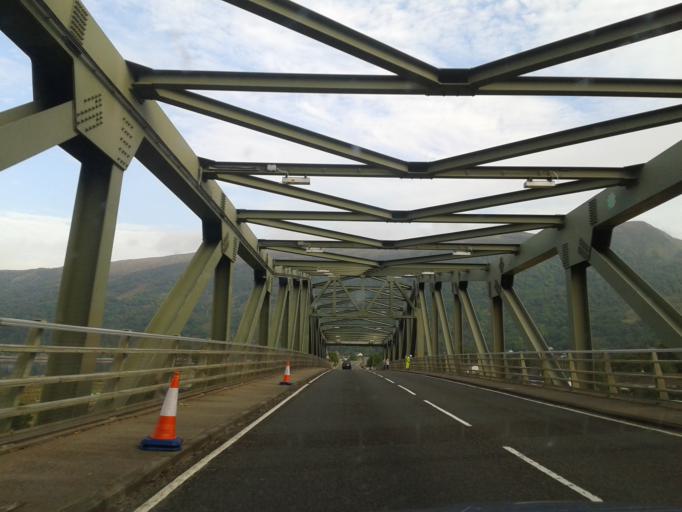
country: GB
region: Scotland
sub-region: Highland
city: Fort William
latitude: 56.6888
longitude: -5.1825
